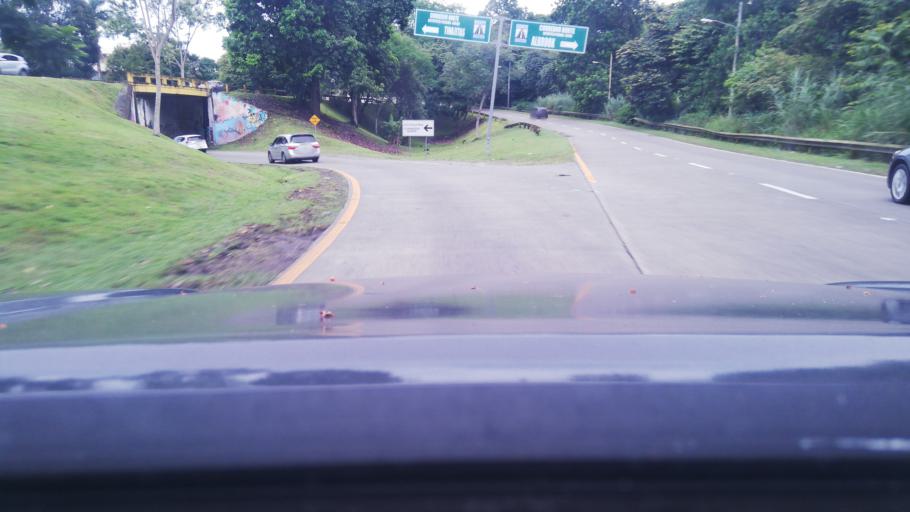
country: PA
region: Panama
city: Panama
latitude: 9.0025
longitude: -79.5454
